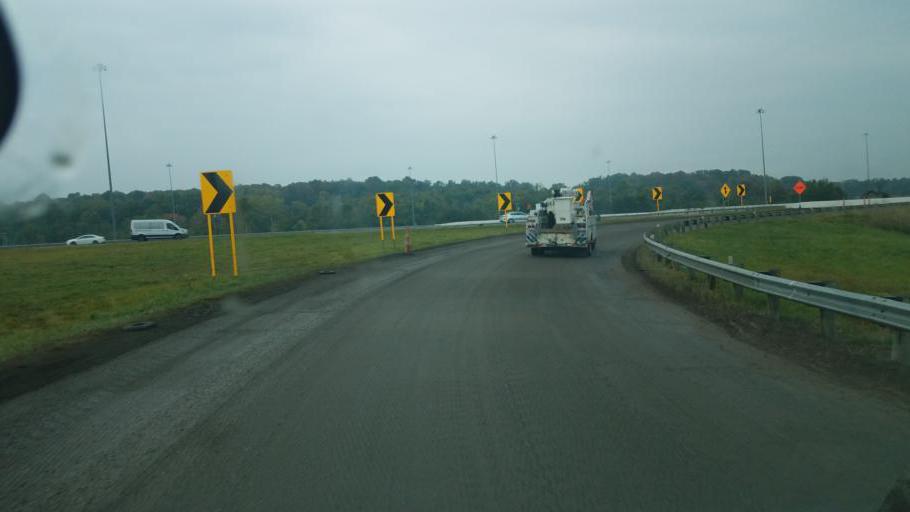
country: US
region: Ohio
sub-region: Richland County
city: Lincoln Heights
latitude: 40.7809
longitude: -82.4122
